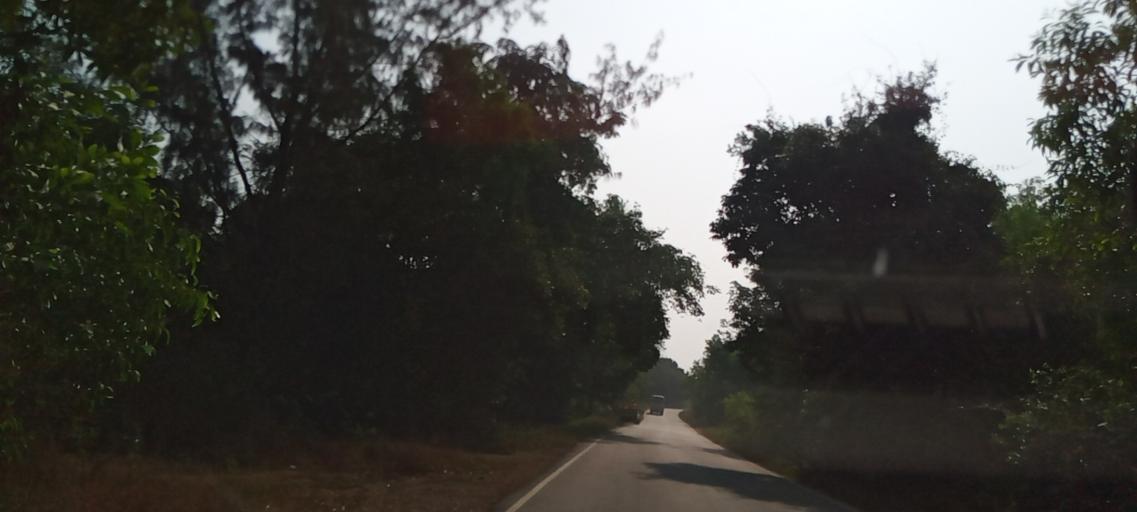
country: IN
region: Karnataka
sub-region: Udupi
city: Coondapoor
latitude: 13.5156
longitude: 74.7920
